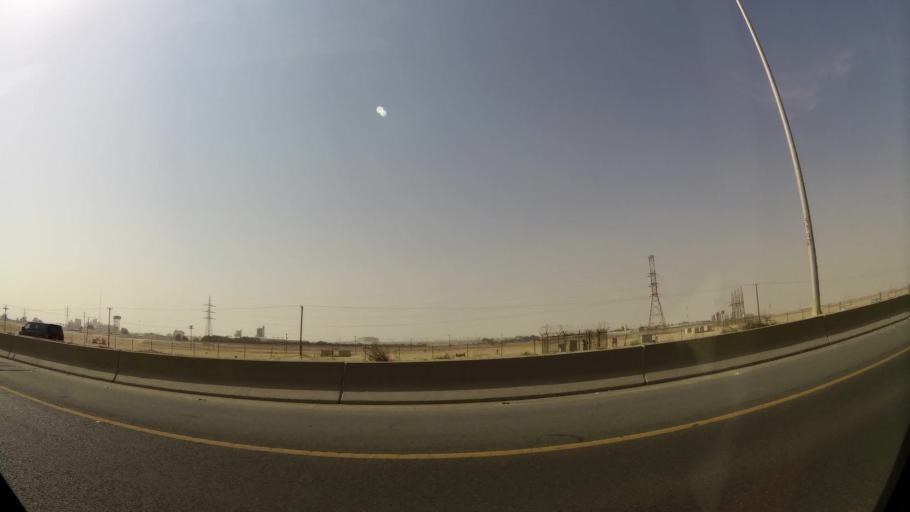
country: KW
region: Al Ahmadi
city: Al Fahahil
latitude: 29.0234
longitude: 48.1259
